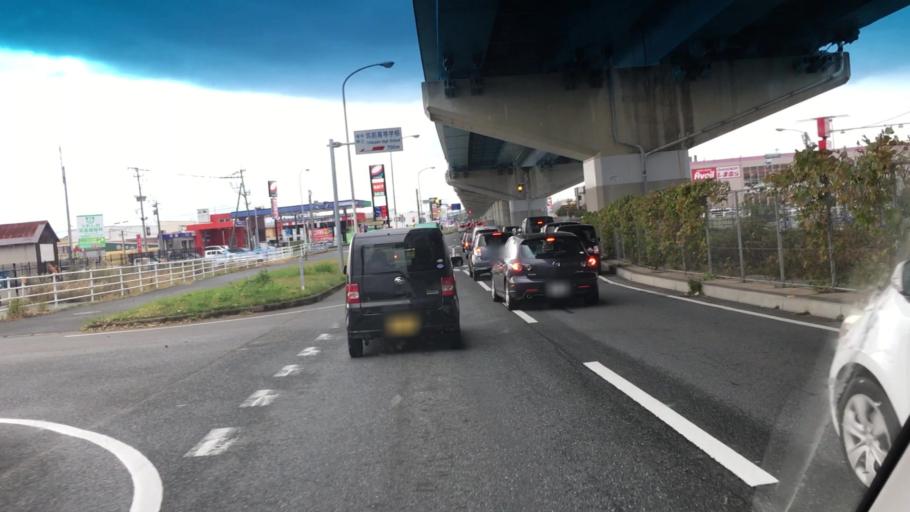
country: JP
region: Fukuoka
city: Maebaru-chuo
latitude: 33.5662
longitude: 130.2442
